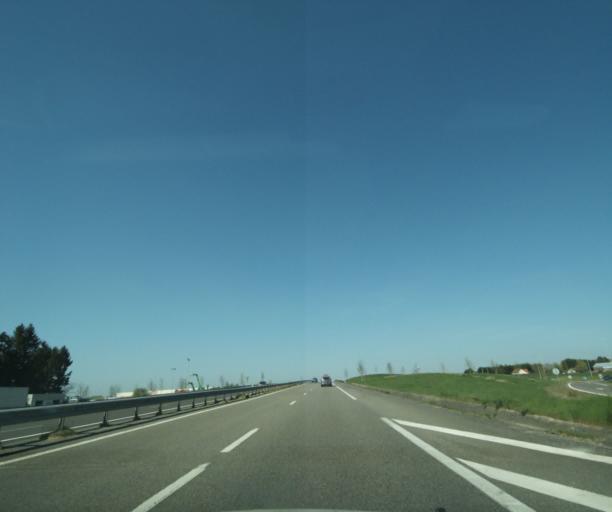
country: FR
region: Bourgogne
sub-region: Departement de la Nievre
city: Cosne-Cours-sur-Loire
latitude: 47.3813
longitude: 2.9231
